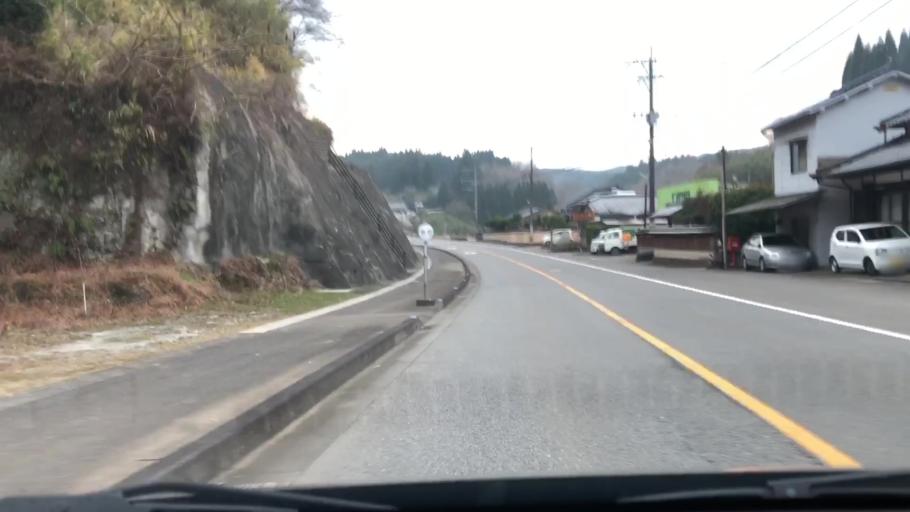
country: JP
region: Oita
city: Usuki
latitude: 33.0075
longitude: 131.6469
